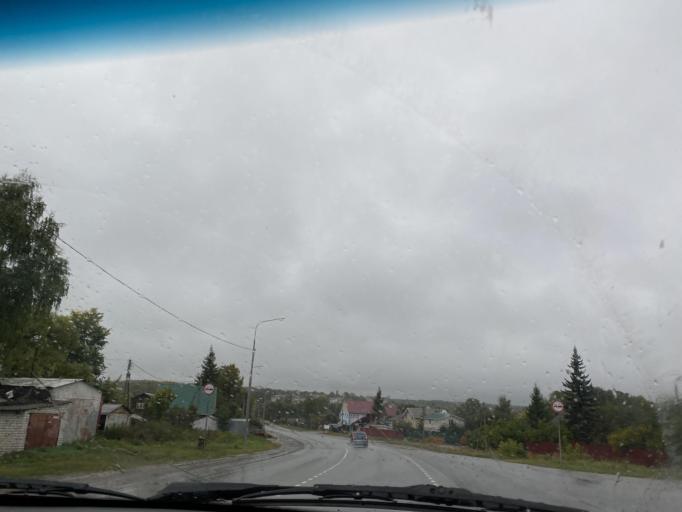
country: RU
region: Rjazan
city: Starozhilovo
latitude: 54.4387
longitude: 39.8982
